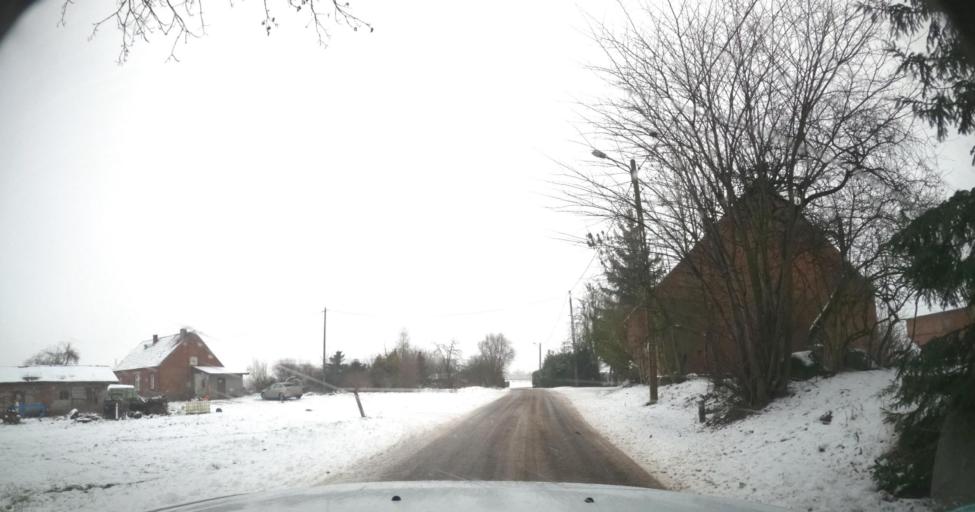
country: PL
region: West Pomeranian Voivodeship
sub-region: Powiat kamienski
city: Golczewo
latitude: 53.7912
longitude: 14.9594
